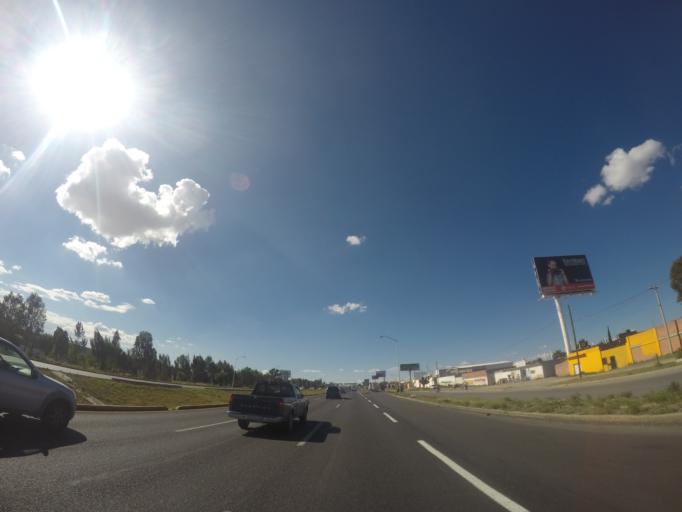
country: MX
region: San Luis Potosi
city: La Pila
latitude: 22.0771
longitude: -100.8745
